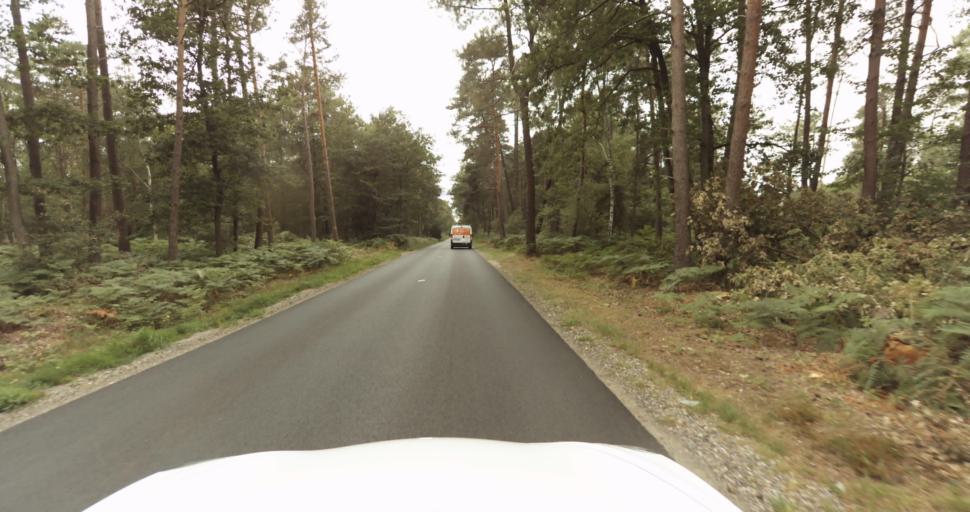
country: FR
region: Haute-Normandie
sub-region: Departement de l'Eure
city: Saint-Sebastien-de-Morsent
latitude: 48.9861
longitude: 1.0622
